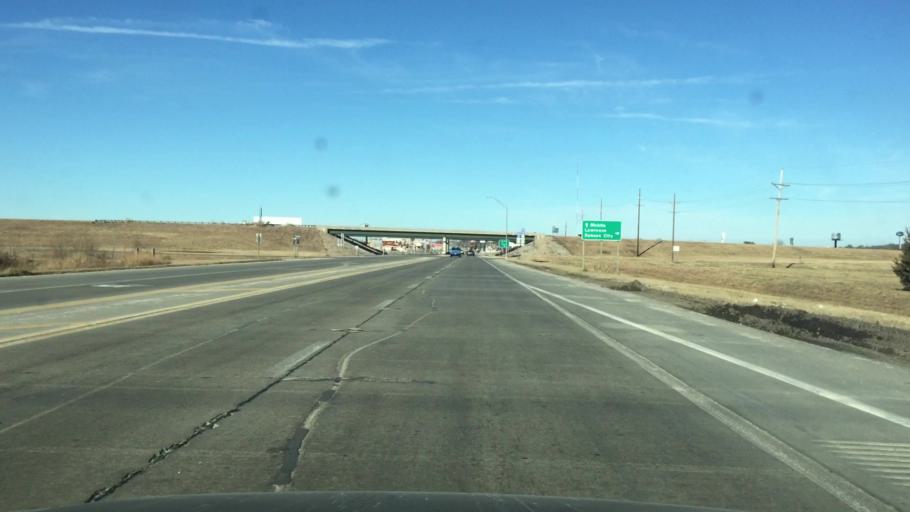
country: US
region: Kansas
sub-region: Franklin County
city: Ottawa
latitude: 38.5728
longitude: -95.2677
